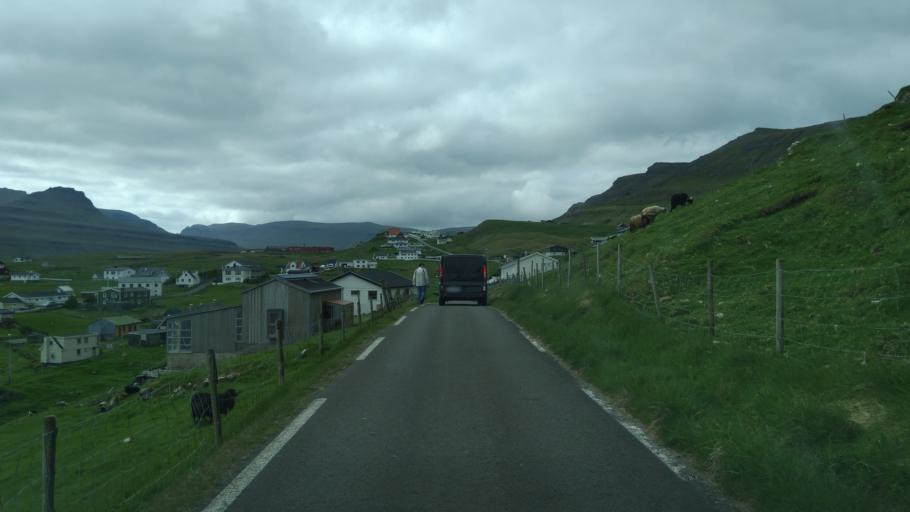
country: FO
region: Suduroy
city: Tvoroyri
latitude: 61.5463
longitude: -6.7709
